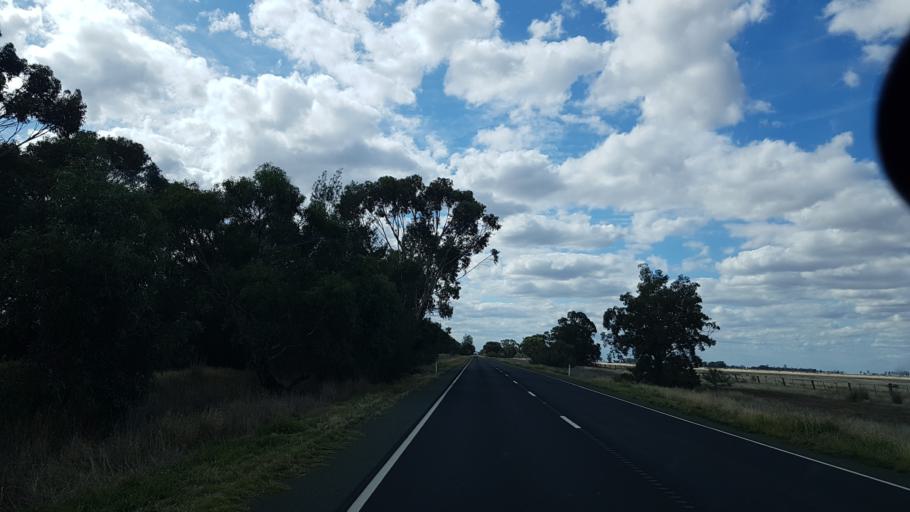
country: AU
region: Victoria
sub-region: Swan Hill
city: Swan Hill
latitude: -35.9861
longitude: 143.9456
